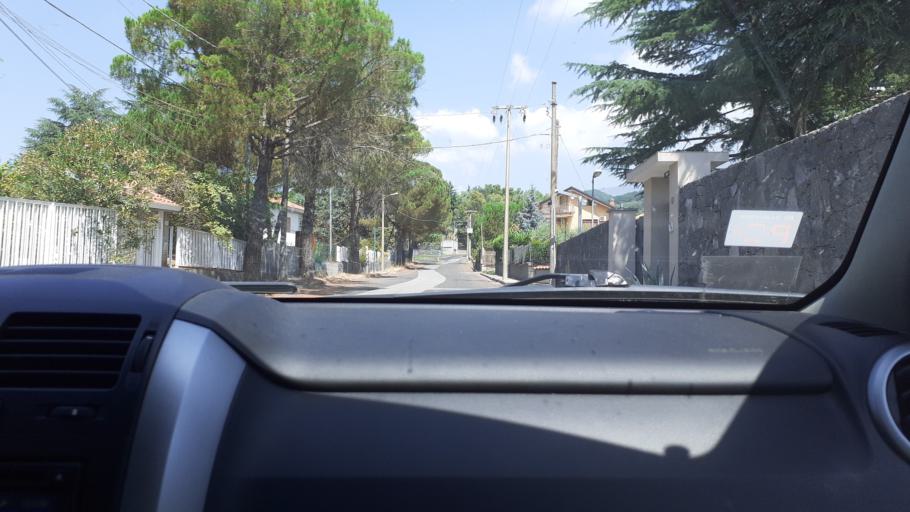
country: IT
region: Sicily
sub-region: Catania
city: Nicolosi
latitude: 37.6234
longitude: 15.0258
